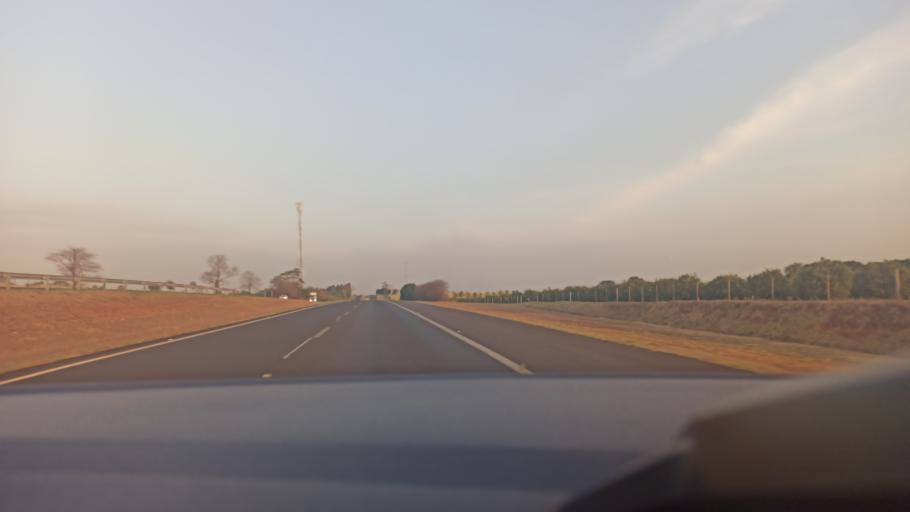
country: BR
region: Sao Paulo
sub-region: Taquaritinga
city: Taquaritinga
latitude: -21.4061
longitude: -48.6987
